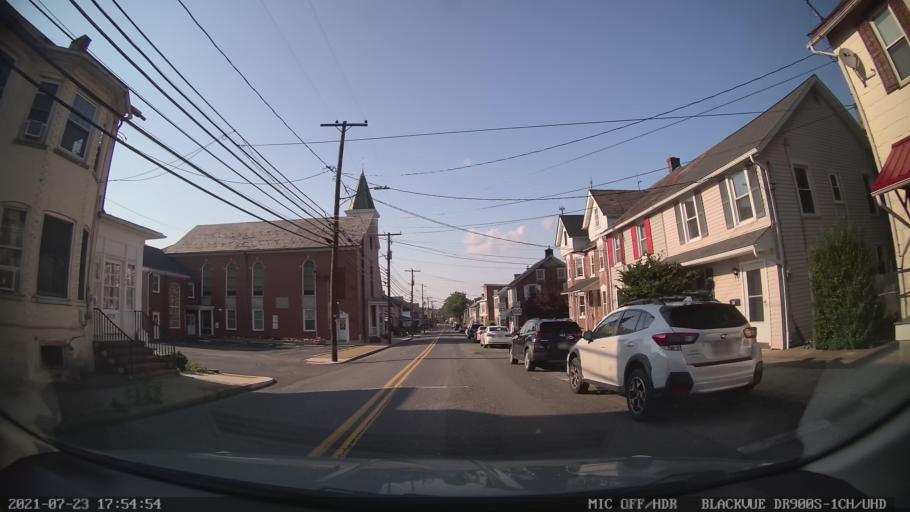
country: US
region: Pennsylvania
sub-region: Lehigh County
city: Macungie
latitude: 40.5126
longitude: -75.5554
